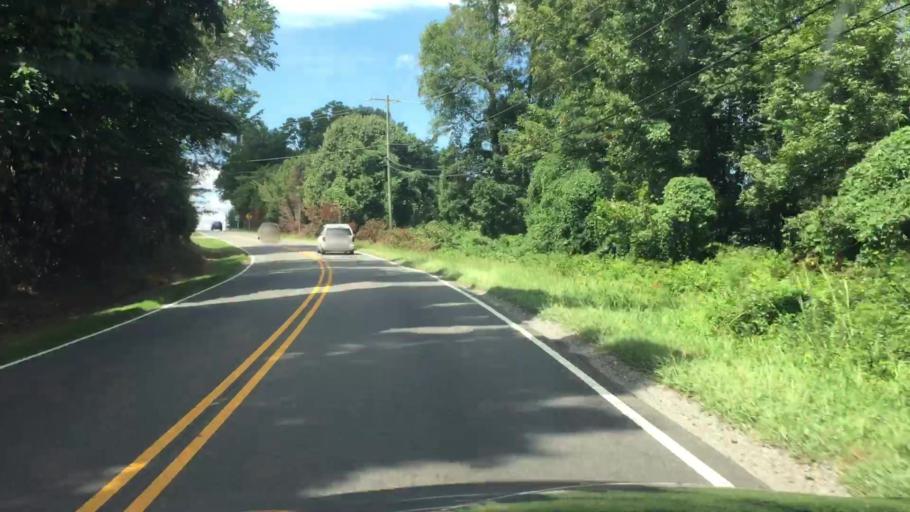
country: US
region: North Carolina
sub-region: Iredell County
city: Mooresville
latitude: 35.5771
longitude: -80.8460
